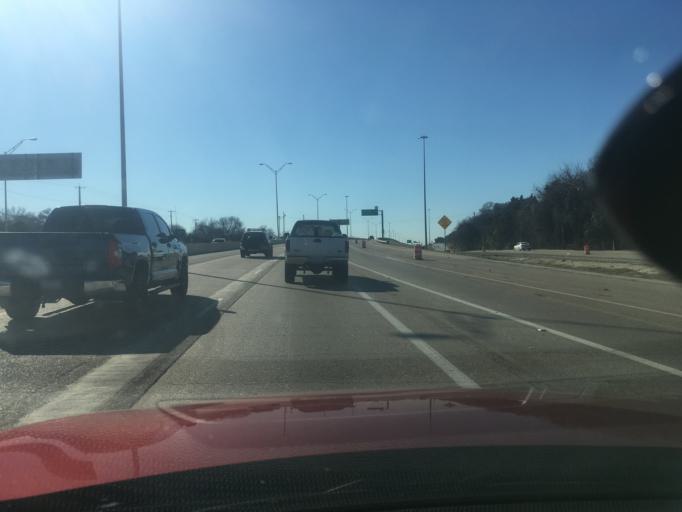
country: US
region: Texas
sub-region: Dallas County
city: Cockrell Hill
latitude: 32.6870
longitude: -96.8482
